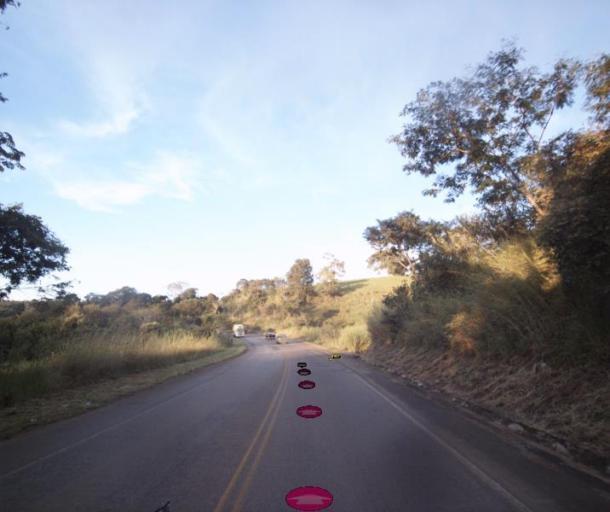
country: BR
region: Goias
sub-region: Abadiania
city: Abadiania
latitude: -16.1159
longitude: -48.8878
